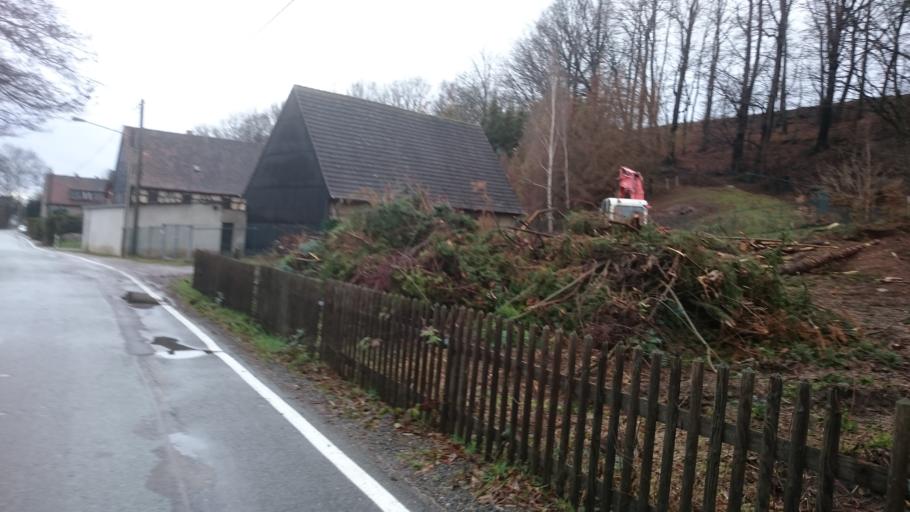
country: DE
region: Saxony
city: Zwickau
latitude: 50.7560
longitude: 12.5156
